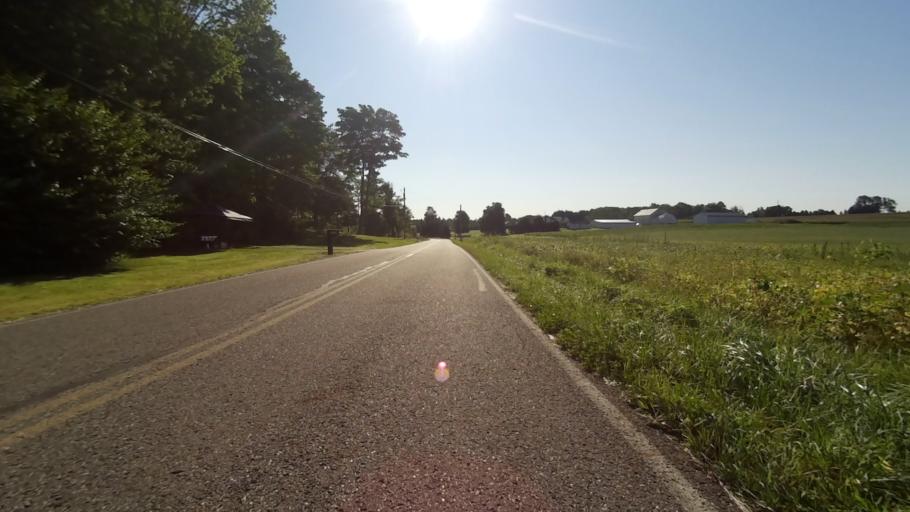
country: US
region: Ohio
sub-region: Portage County
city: Mantua
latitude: 41.2930
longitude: -81.2705
